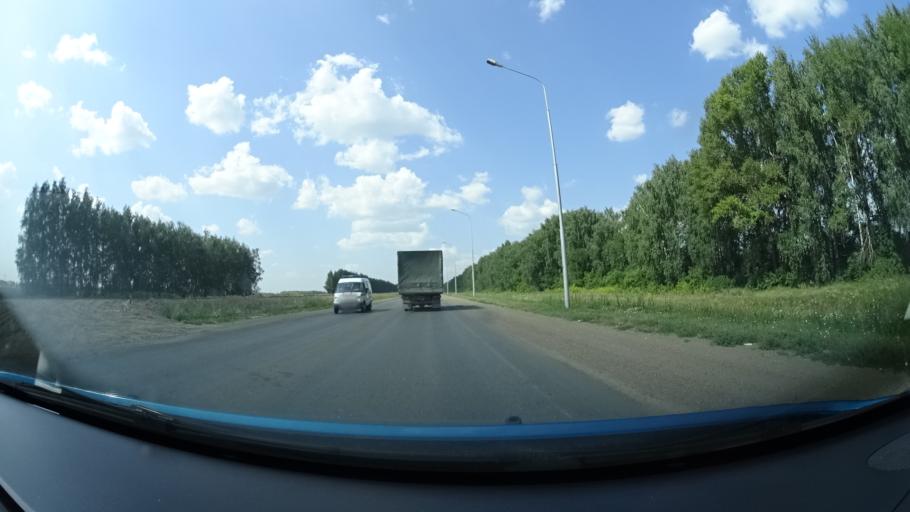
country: RU
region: Bashkortostan
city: Buzdyak
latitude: 54.6456
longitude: 54.5573
